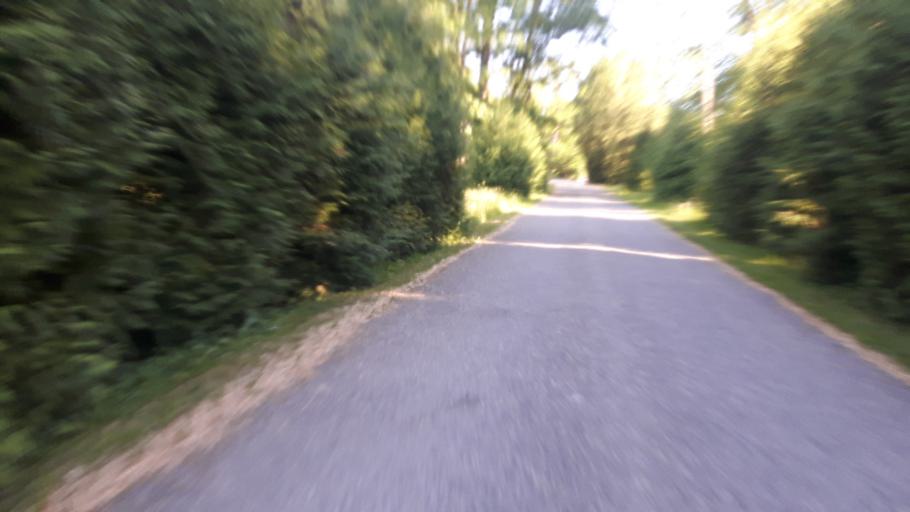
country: EE
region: Raplamaa
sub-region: Kehtna vald
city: Kehtna
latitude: 58.9237
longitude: 24.8726
